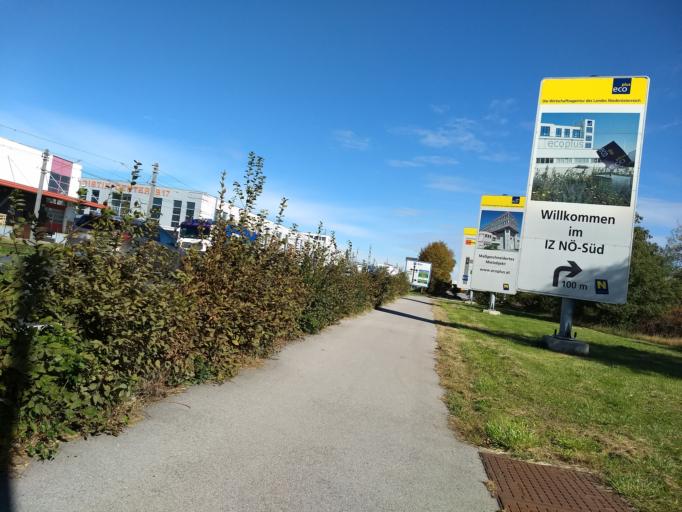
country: AT
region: Lower Austria
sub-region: Politischer Bezirk Modling
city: Wiener Neudorf
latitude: 48.0744
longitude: 16.3120
